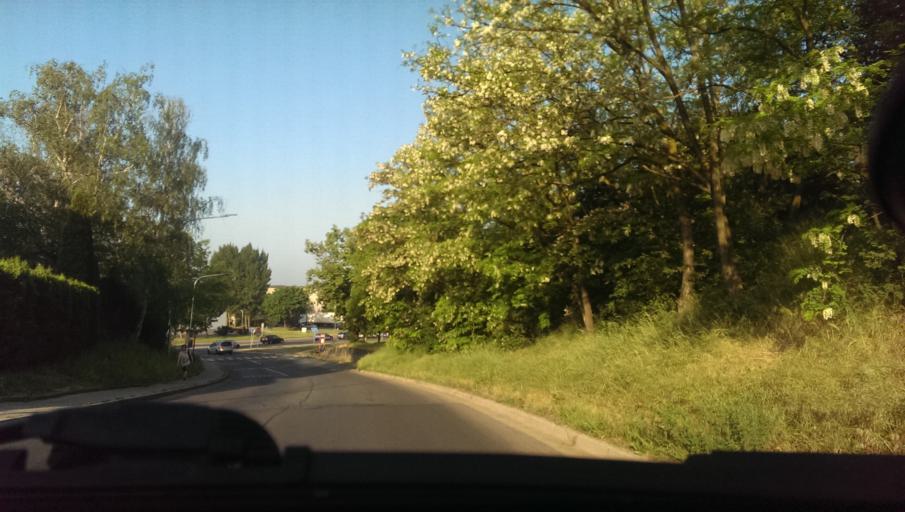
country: CZ
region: Zlin
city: Kunovice
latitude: 49.0573
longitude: 17.4687
